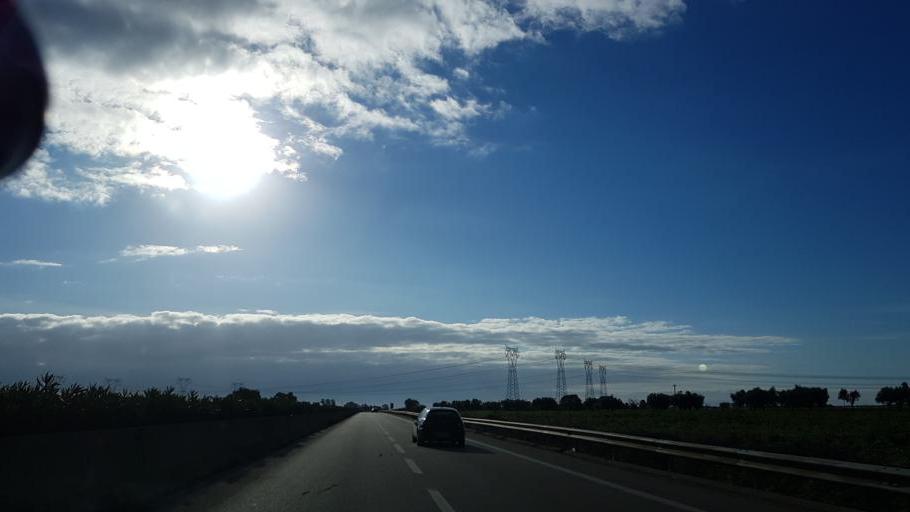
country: IT
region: Apulia
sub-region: Provincia di Brindisi
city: Tuturano
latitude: 40.5649
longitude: 17.9872
